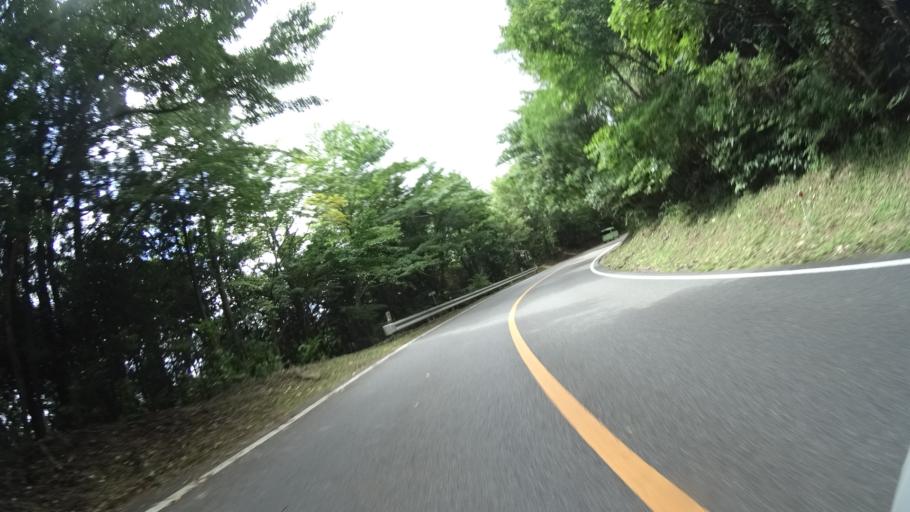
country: JP
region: Oita
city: Tsukawaki
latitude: 33.1986
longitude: 131.2881
